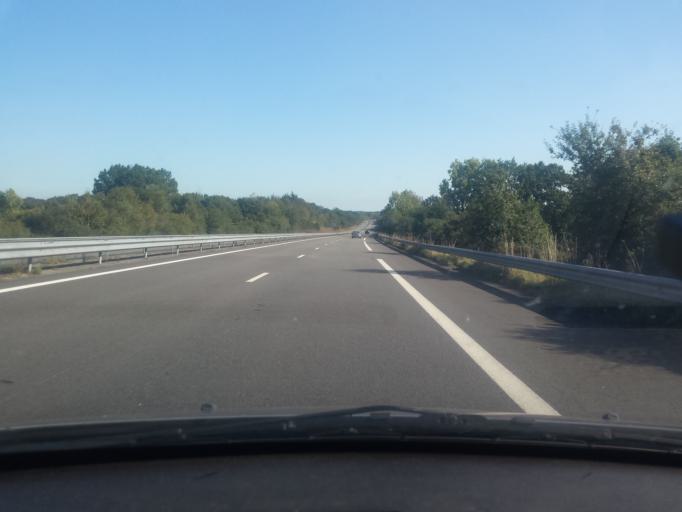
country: FR
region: Brittany
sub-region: Departement du Morbihan
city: Naizin
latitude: 47.9957
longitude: -2.8860
